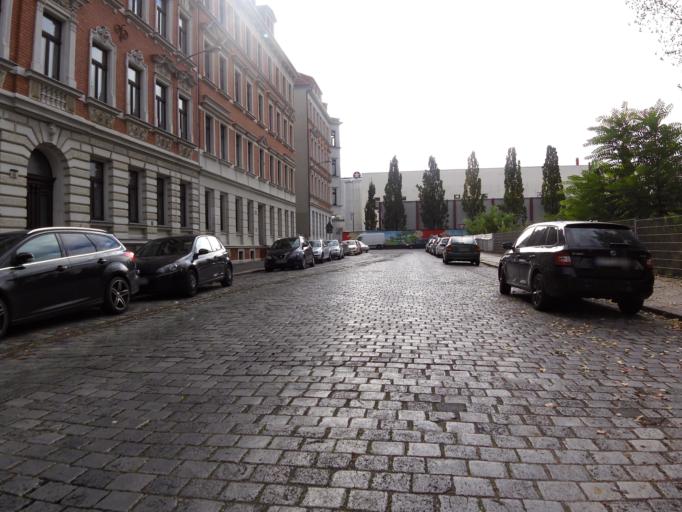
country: DE
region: Saxony
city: Leipzig
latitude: 51.3330
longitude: 12.4021
